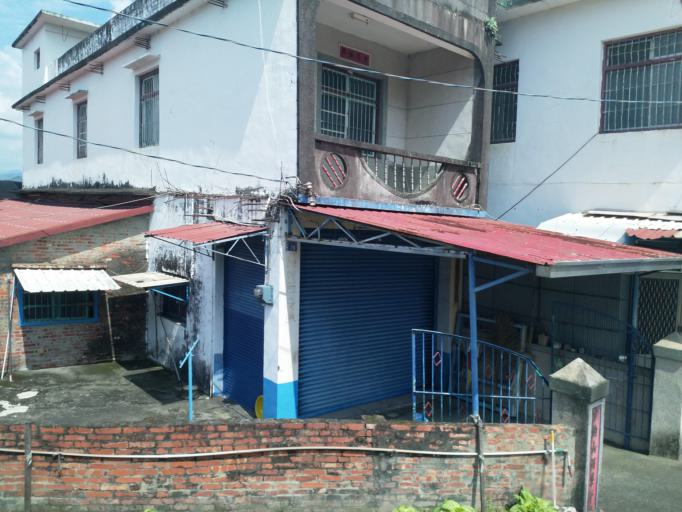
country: TW
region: Taiwan
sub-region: Pingtung
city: Pingtung
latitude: 22.8769
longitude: 120.5721
